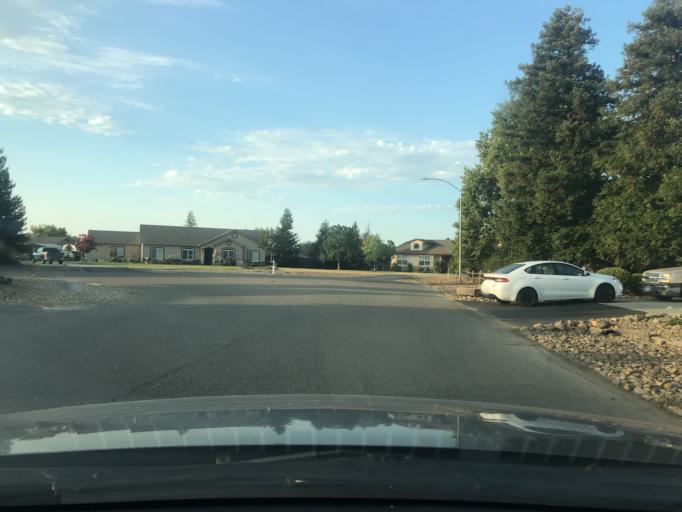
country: US
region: California
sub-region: Merced County
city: Merced
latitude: 37.3340
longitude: -120.5392
